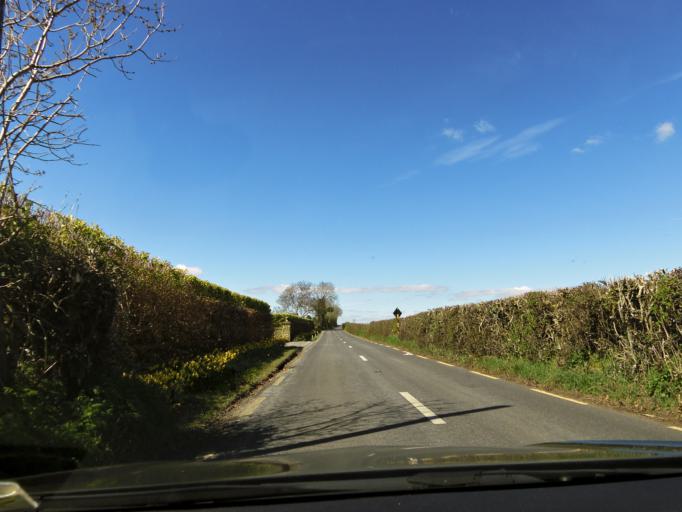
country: IE
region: Leinster
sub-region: Kildare
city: Moone
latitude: 52.9788
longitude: -6.7792
